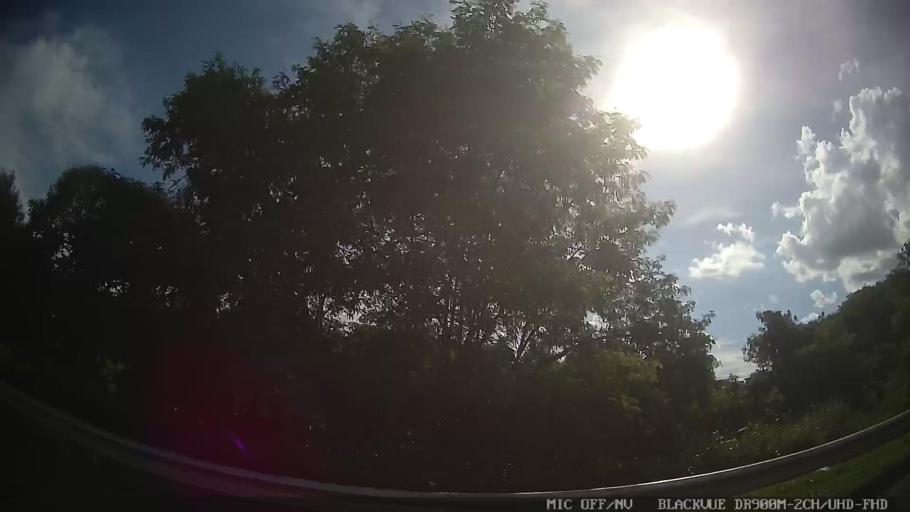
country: BR
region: Sao Paulo
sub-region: Laranjal Paulista
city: Laranjal Paulista
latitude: -23.0472
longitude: -47.8250
